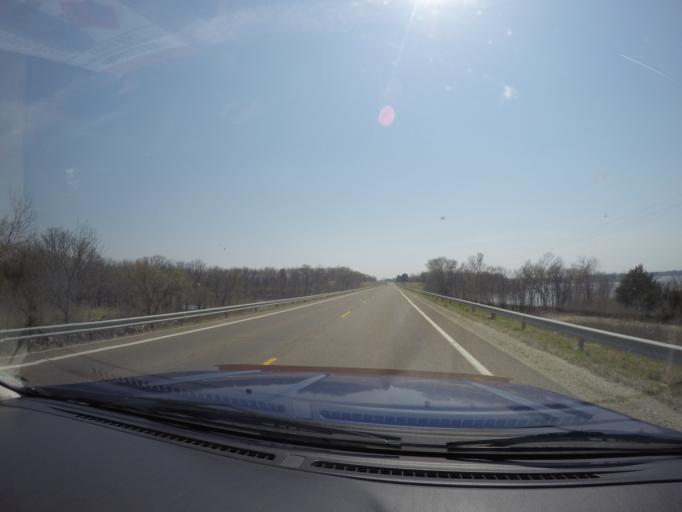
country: US
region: Kansas
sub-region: Morris County
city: Council Grove
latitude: 38.7066
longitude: -96.4973
